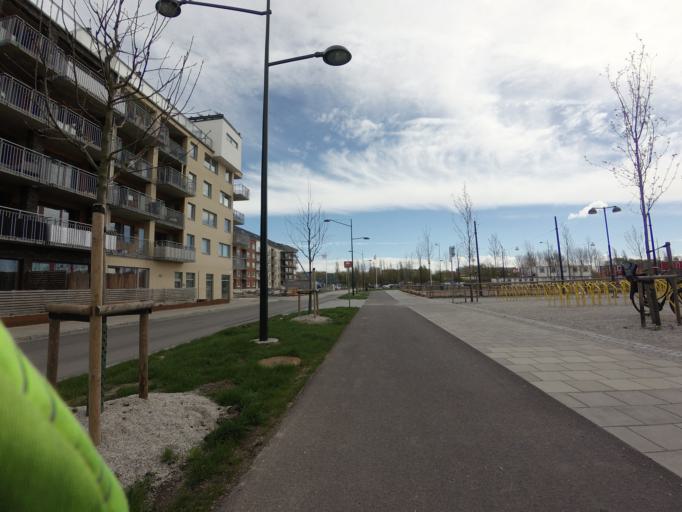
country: SE
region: Skane
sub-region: Malmo
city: Bunkeflostrand
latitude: 55.5597
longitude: 12.9812
